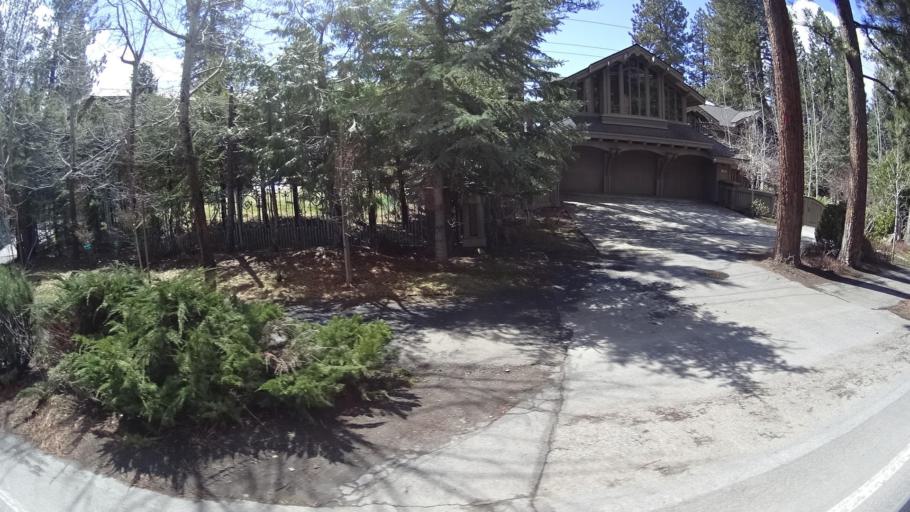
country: US
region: Nevada
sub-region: Washoe County
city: Incline Village
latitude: 39.2414
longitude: -119.9504
